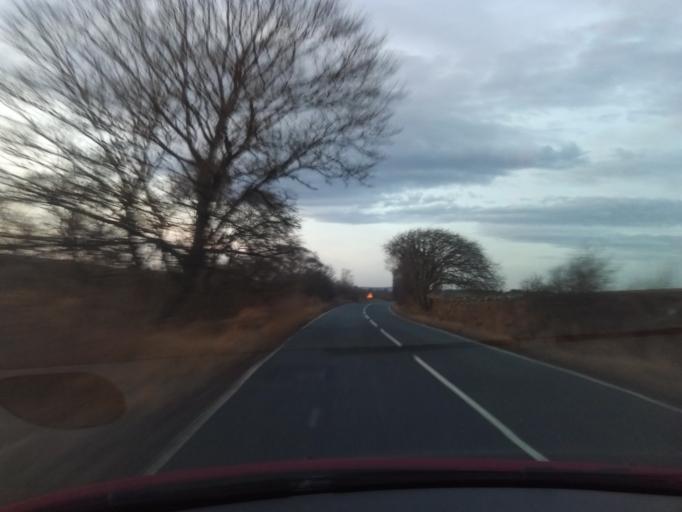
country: GB
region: England
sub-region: Northumberland
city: Otterburn
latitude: 55.2417
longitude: -2.2126
